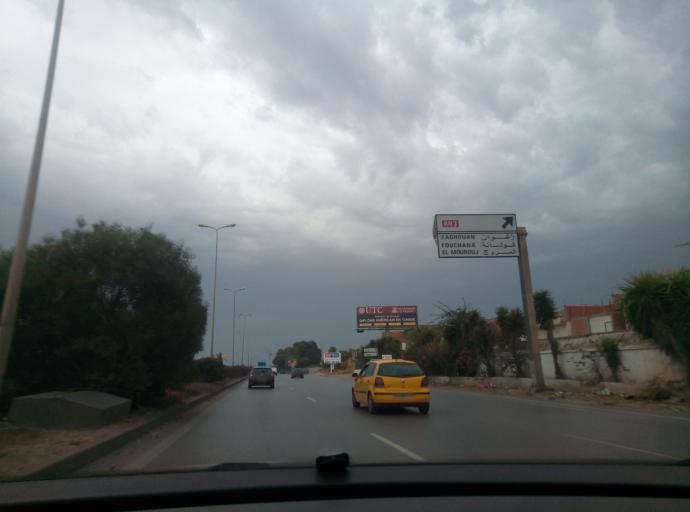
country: TN
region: Bin 'Arus
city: Ben Arous
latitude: 36.7500
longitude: 10.2064
